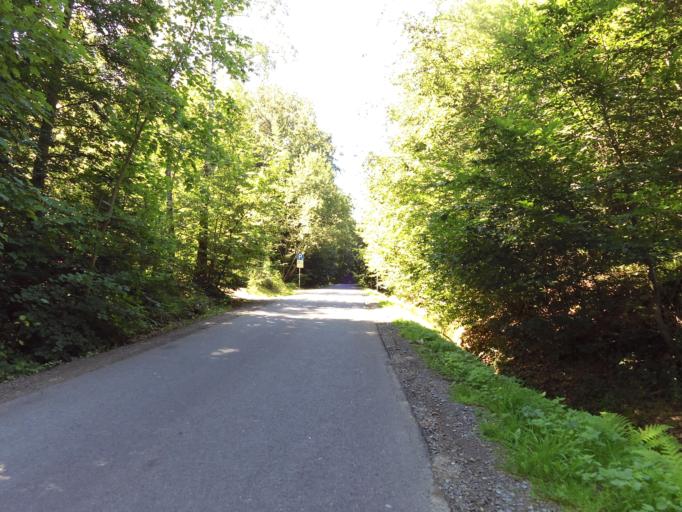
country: DE
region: Hesse
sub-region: Regierungsbezirk Darmstadt
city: Erbach
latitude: 49.6773
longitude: 8.9785
